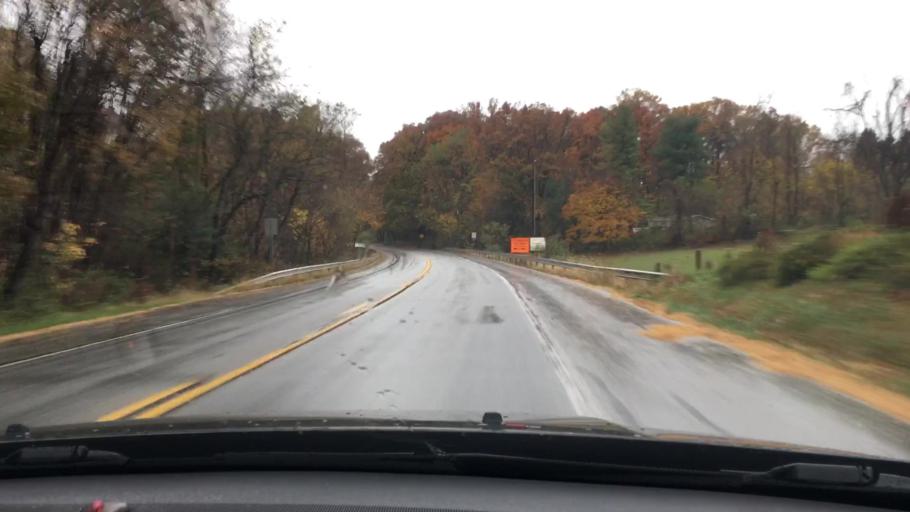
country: US
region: Pennsylvania
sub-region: York County
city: Susquehanna Trails
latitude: 39.8349
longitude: -76.3095
